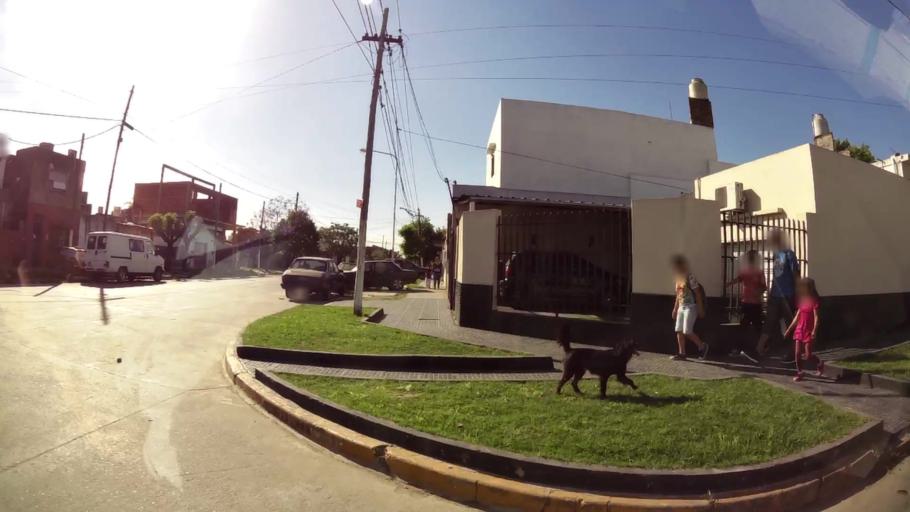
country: AR
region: Buenos Aires
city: Hurlingham
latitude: -34.5609
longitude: -58.6223
